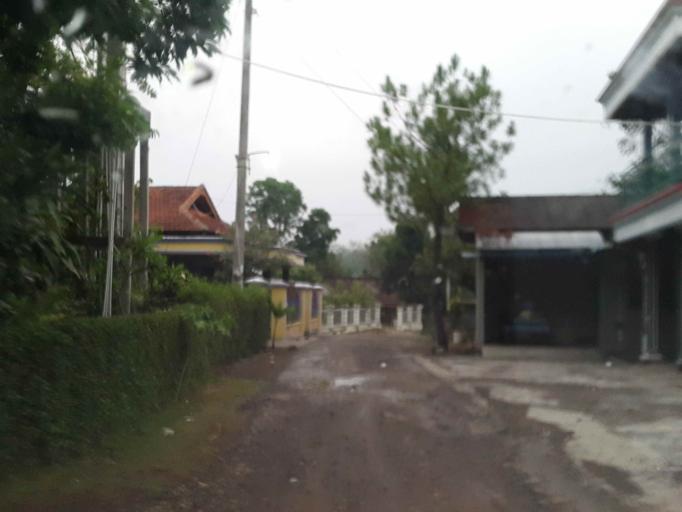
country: ID
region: Central Java
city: Sragen
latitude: -7.5370
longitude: 111.0043
